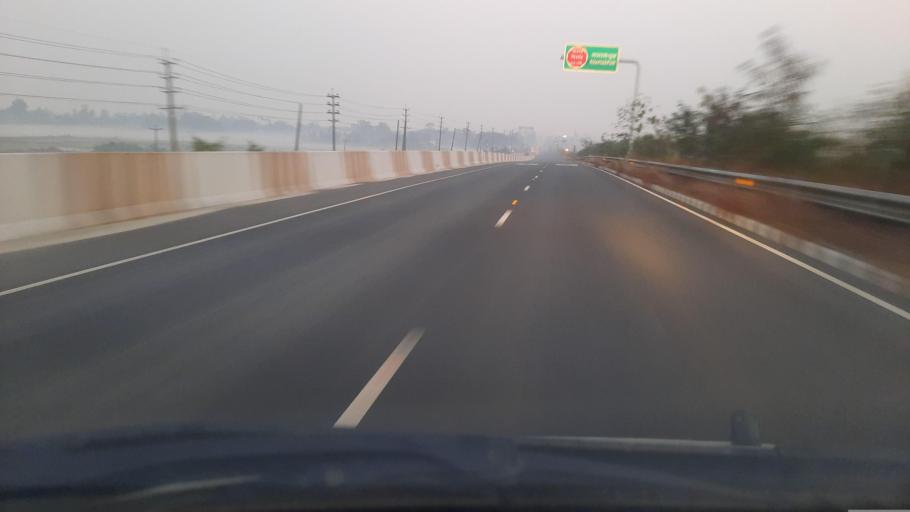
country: BD
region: Dhaka
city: Dohar
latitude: 23.5057
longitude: 90.2746
